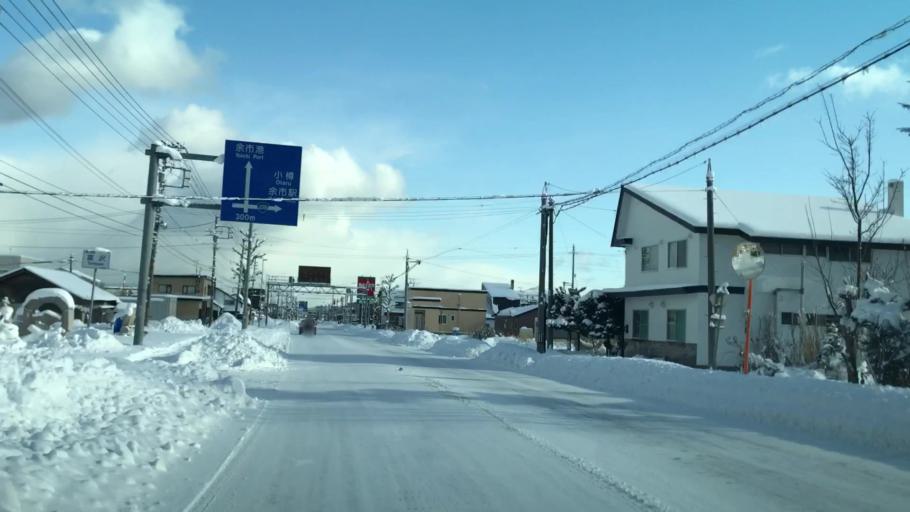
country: JP
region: Hokkaido
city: Yoichi
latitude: 43.2080
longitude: 140.7672
